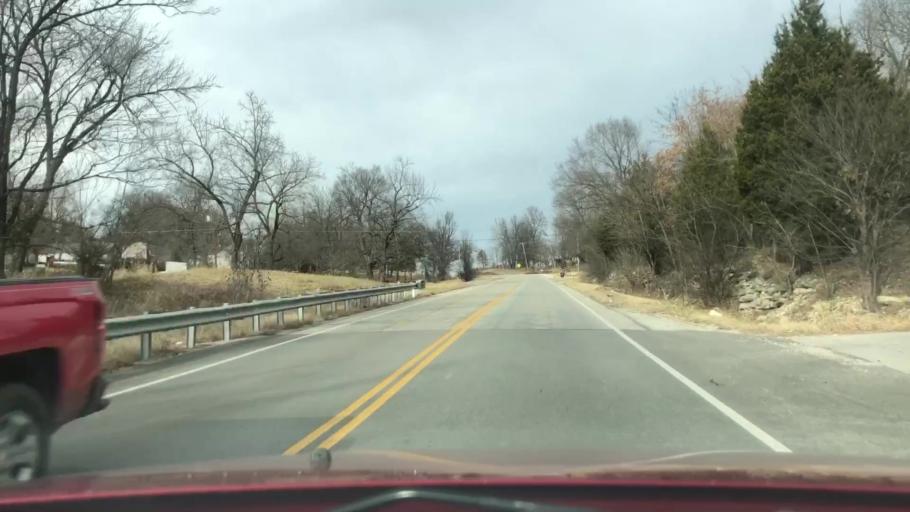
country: US
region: Missouri
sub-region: Greene County
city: Springfield
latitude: 37.2765
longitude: -93.2632
